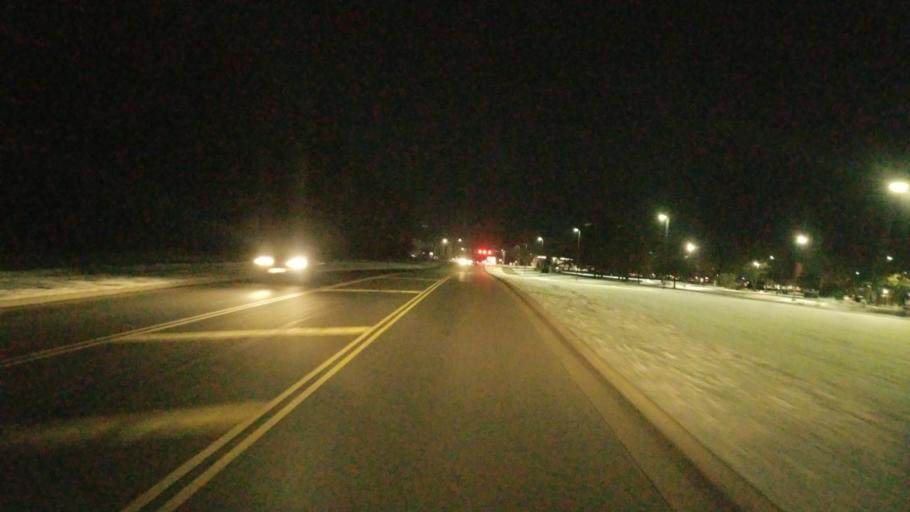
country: US
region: Ohio
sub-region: Marion County
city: Marion
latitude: 40.5774
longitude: -83.0927
